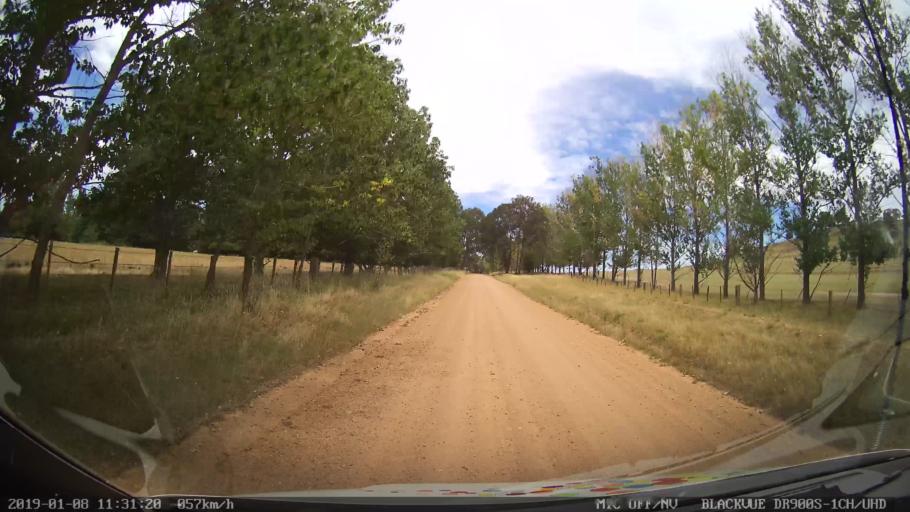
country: AU
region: New South Wales
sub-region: Guyra
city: Guyra
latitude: -30.3120
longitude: 151.5379
